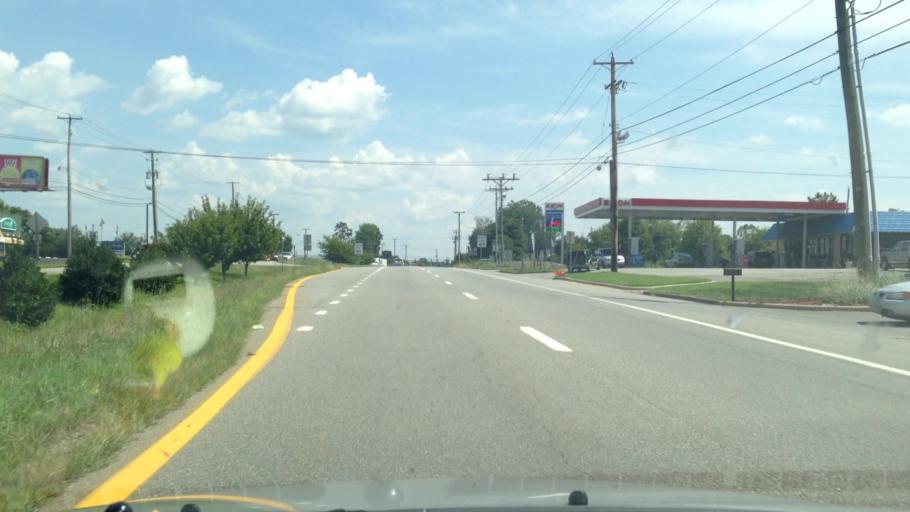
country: US
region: Virginia
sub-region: City of Martinsville
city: Martinsville
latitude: 36.6412
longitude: -79.8619
